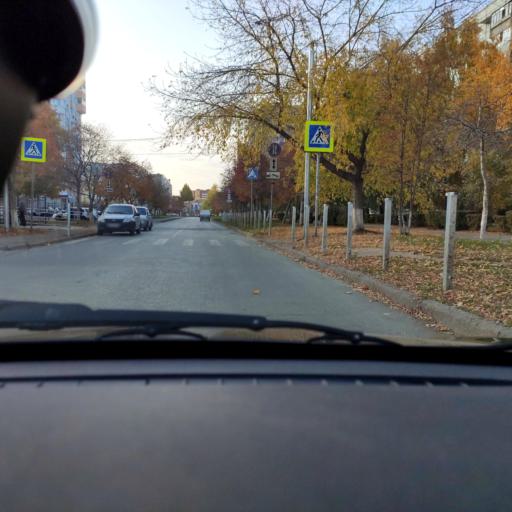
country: RU
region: Samara
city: Tol'yatti
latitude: 53.5429
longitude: 49.3527
